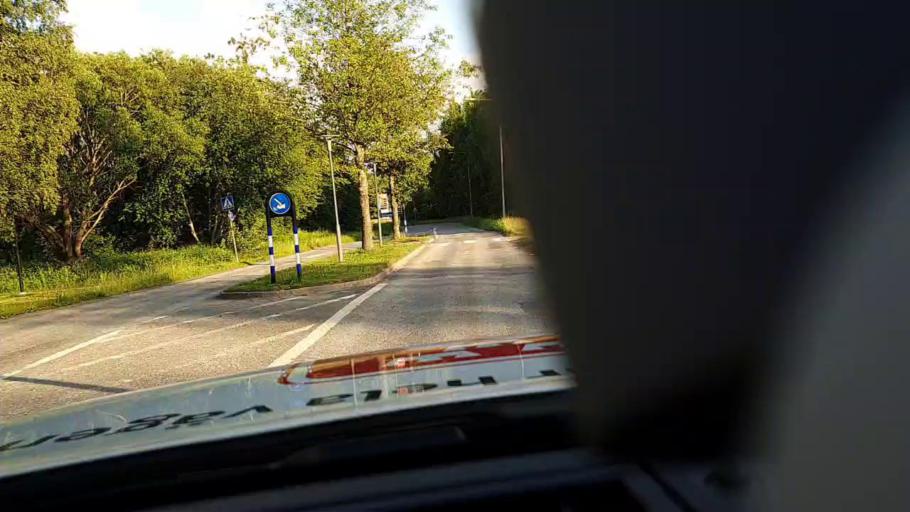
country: SE
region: Stockholm
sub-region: Huddinge Kommun
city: Huddinge
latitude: 59.2428
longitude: 17.9775
